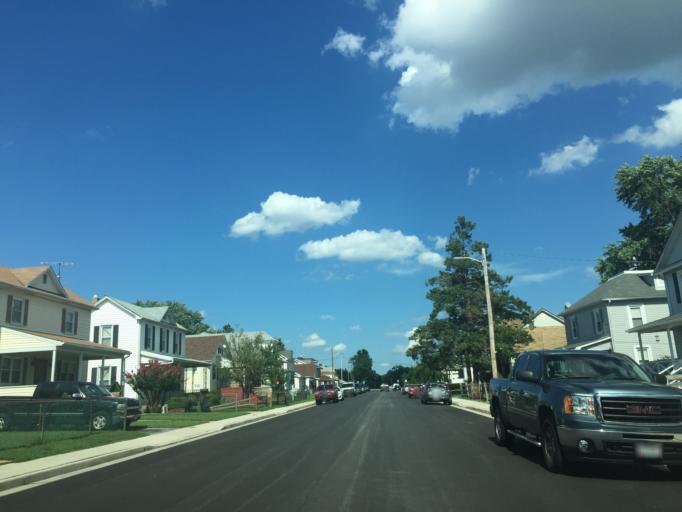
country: US
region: Maryland
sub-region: Baltimore County
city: Essex
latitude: 39.3093
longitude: -76.4765
